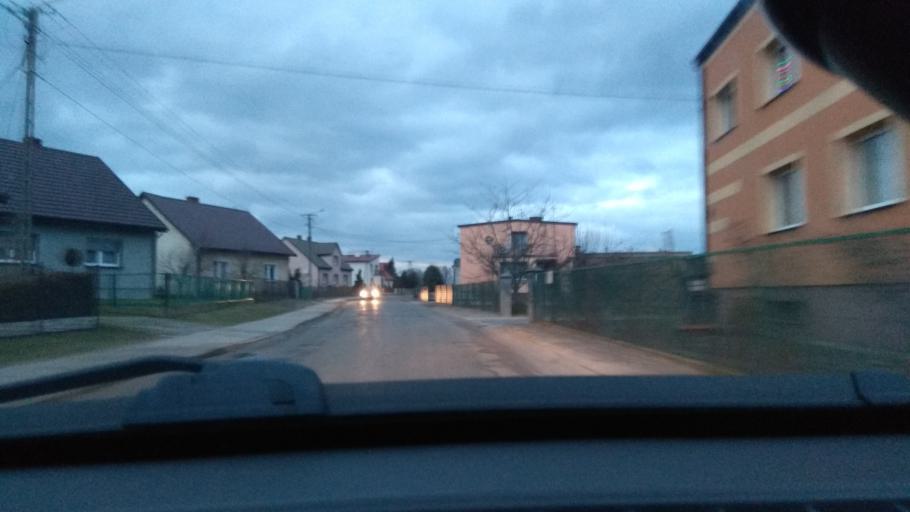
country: PL
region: Lodz Voivodeship
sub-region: Powiat wieruszowski
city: Wieruszow
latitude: 51.3056
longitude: 18.0817
